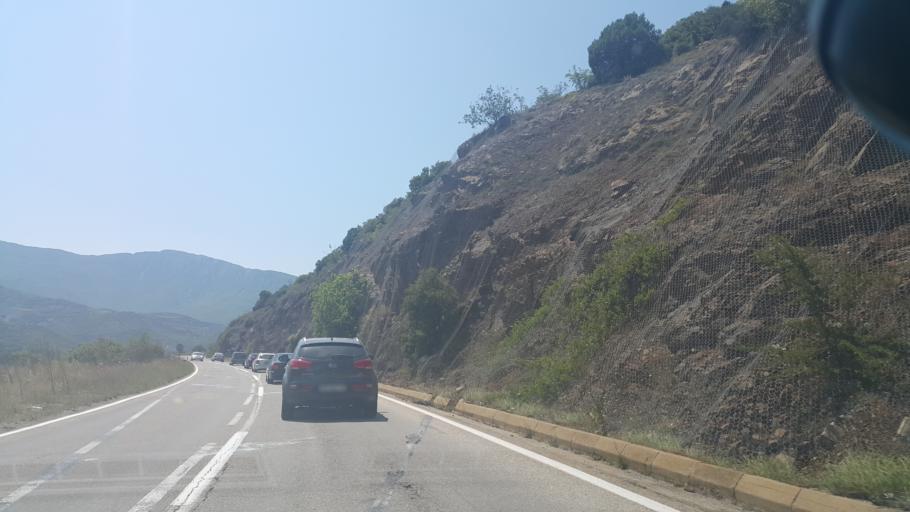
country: MK
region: Demir Kapija
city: Demir Kapija
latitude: 41.3937
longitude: 22.3353
